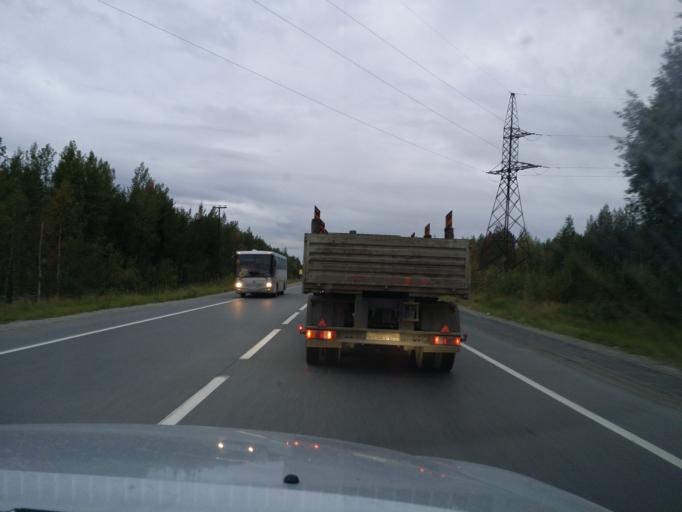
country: RU
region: Khanty-Mansiyskiy Avtonomnyy Okrug
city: Izluchinsk
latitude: 61.0081
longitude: 76.7677
